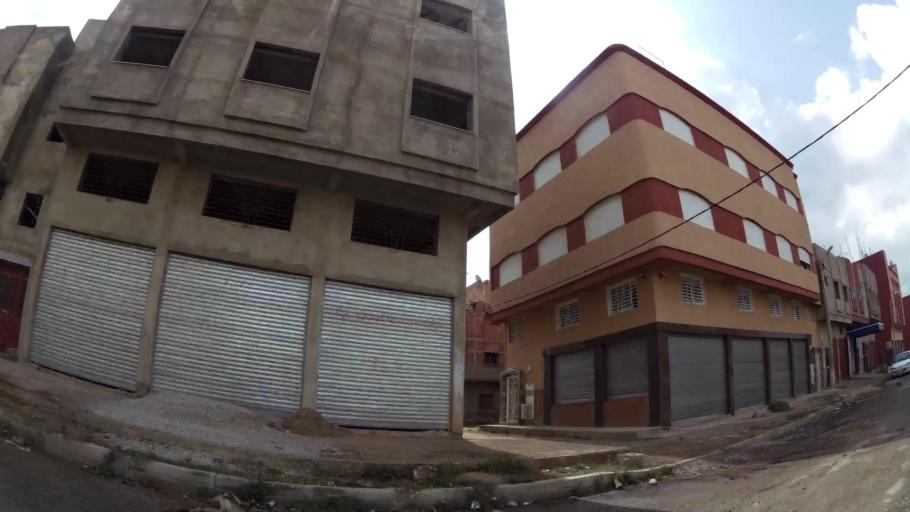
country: MA
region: Rabat-Sale-Zemmour-Zaer
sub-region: Khemisset
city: Tiflet
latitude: 33.8982
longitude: -6.3323
